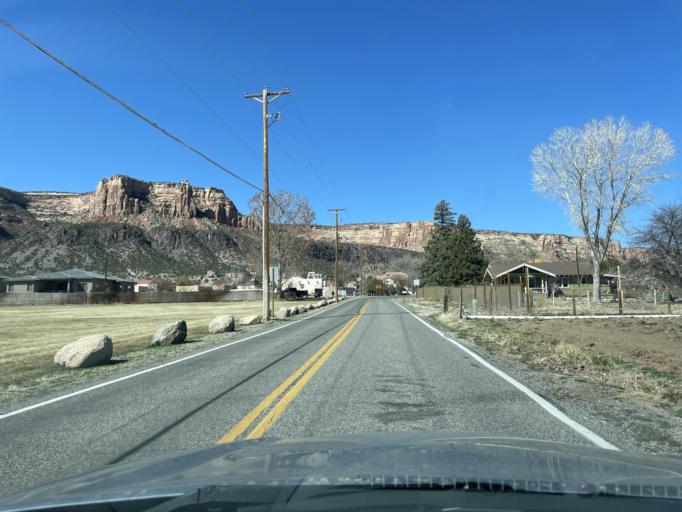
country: US
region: Colorado
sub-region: Mesa County
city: Redlands
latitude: 39.0742
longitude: -108.6626
